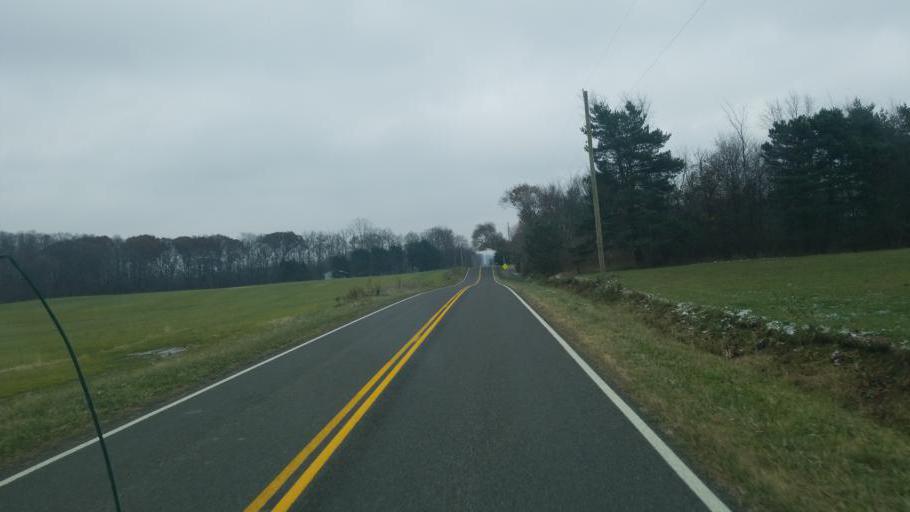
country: US
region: Ohio
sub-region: Medina County
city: Medina
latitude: 41.1359
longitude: -81.9678
